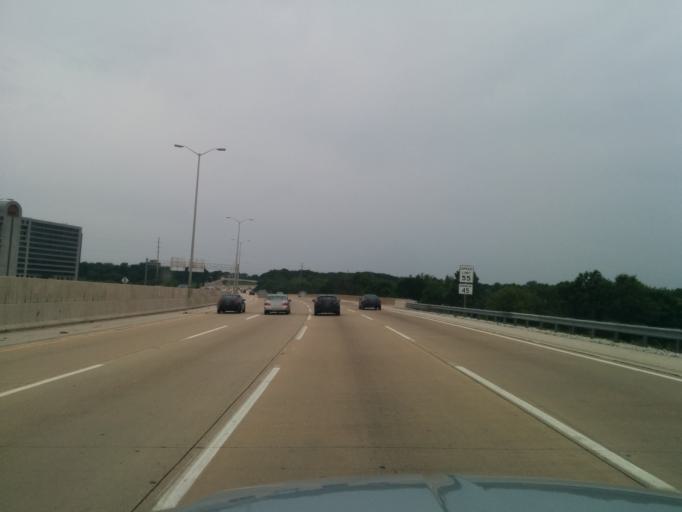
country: US
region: Illinois
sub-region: DuPage County
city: Lisle
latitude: 41.8097
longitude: -88.0761
